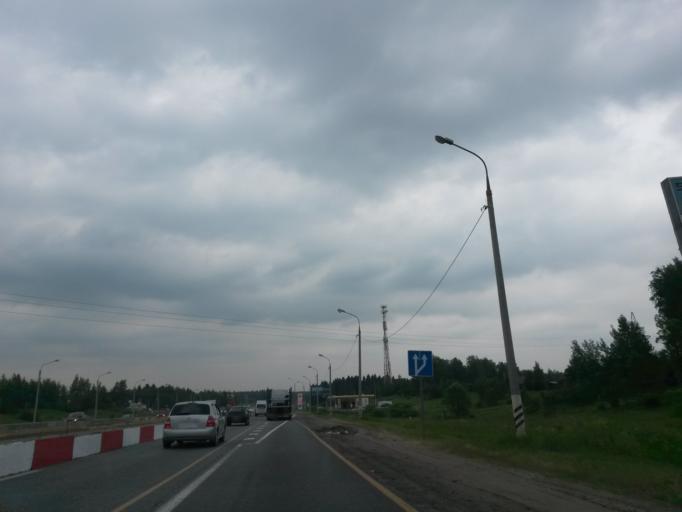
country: RU
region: Moskovskaya
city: Lyubuchany
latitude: 55.2266
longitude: 37.5310
